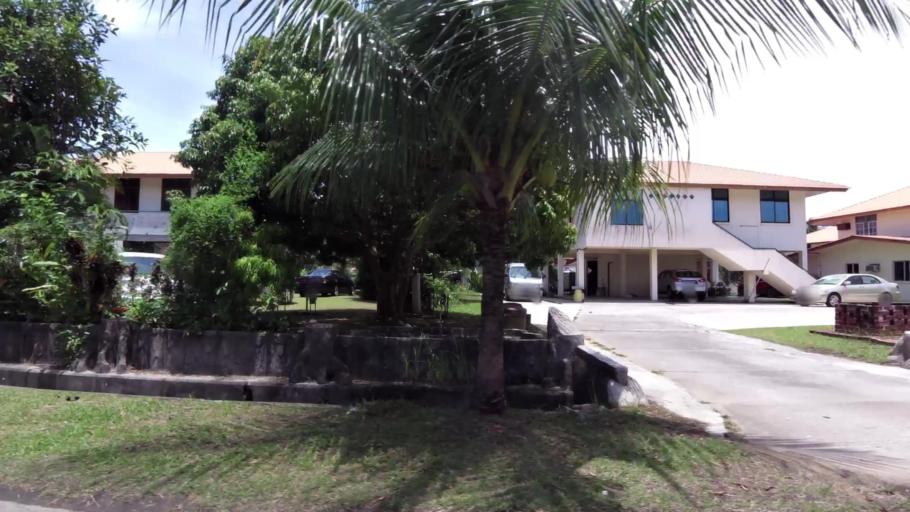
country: BN
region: Belait
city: Kuala Belait
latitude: 4.5889
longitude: 114.2468
